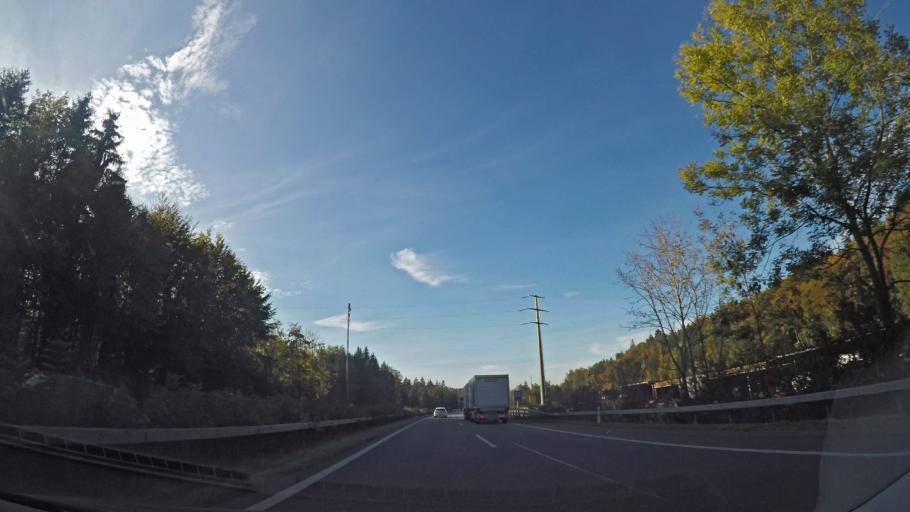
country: CH
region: Bern
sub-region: Thun District
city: Thun
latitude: 46.7137
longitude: 7.6201
